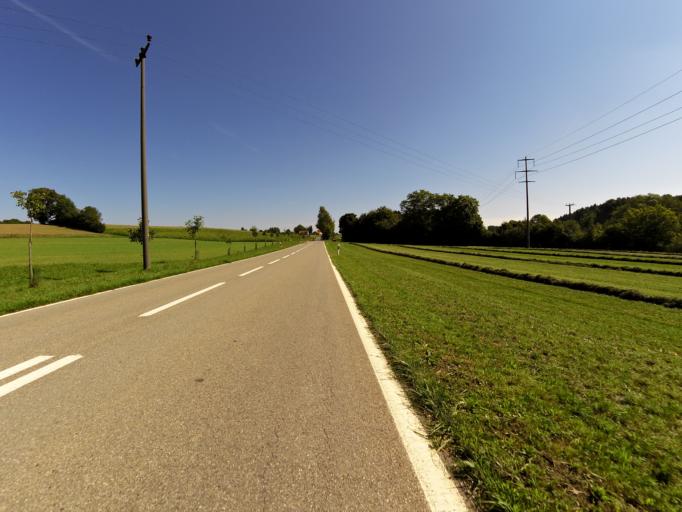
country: CH
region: Thurgau
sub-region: Weinfelden District
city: Maerstetten-Dorf
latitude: 47.6043
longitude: 9.0787
